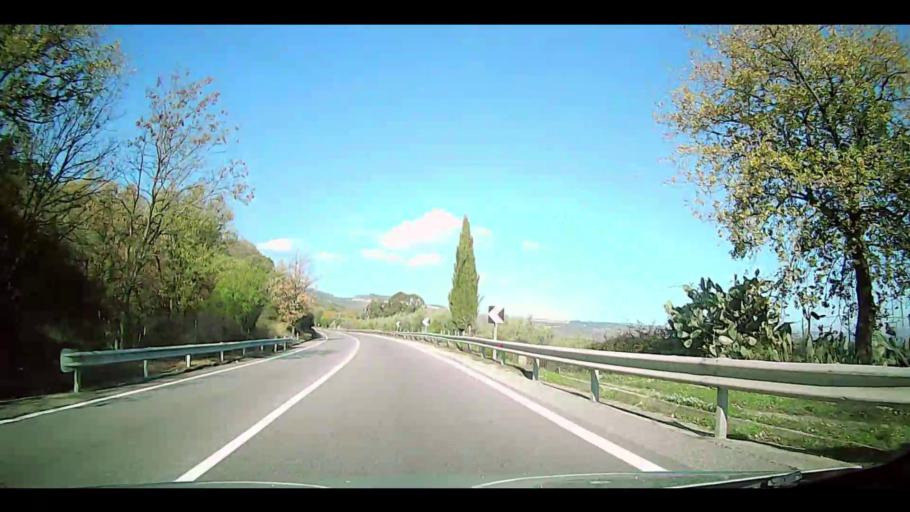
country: IT
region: Calabria
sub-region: Provincia di Crotone
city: Caccuri
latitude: 39.2019
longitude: 16.8106
